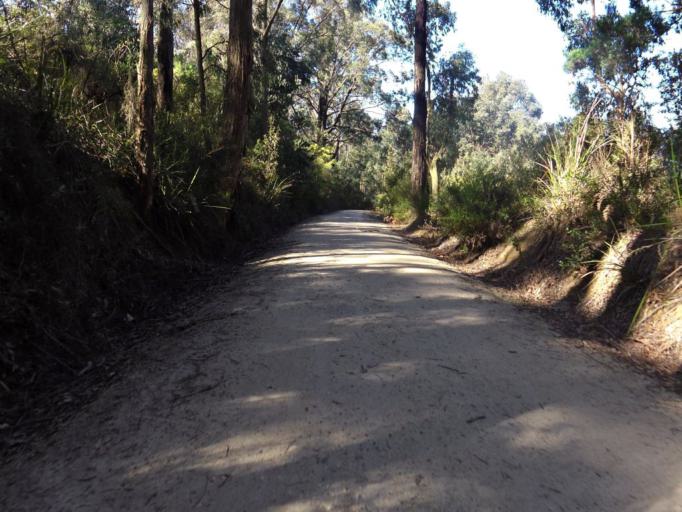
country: AU
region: Victoria
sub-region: Latrobe
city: Moe
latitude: -38.3908
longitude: 146.1819
